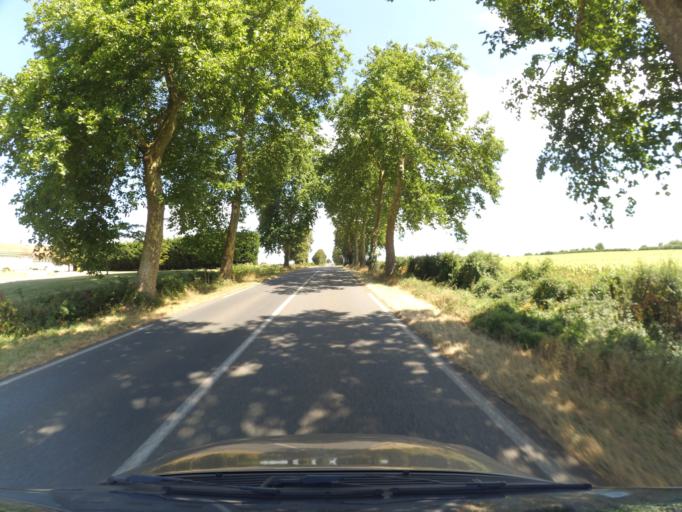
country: FR
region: Poitou-Charentes
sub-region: Departement des Deux-Sevres
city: Pamproux
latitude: 46.4183
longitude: -0.0190
